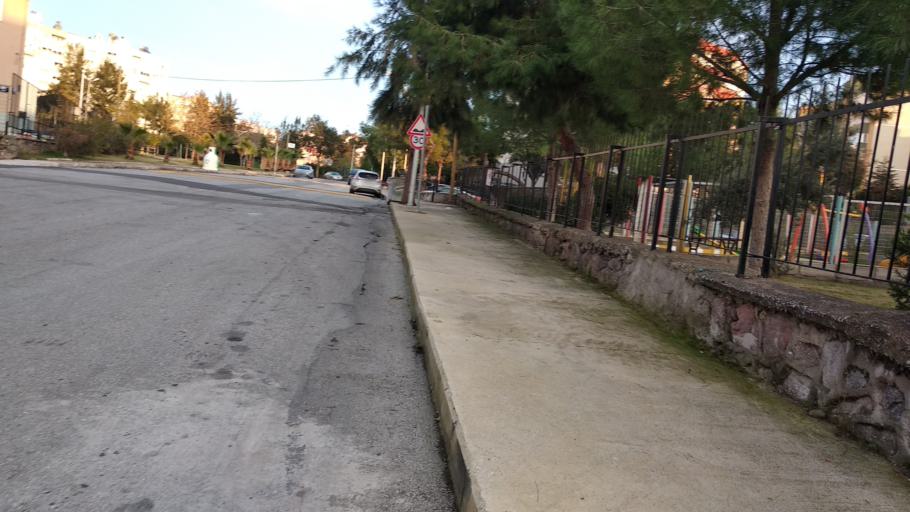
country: TR
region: Izmir
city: Karsiyaka
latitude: 38.4959
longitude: 27.0862
